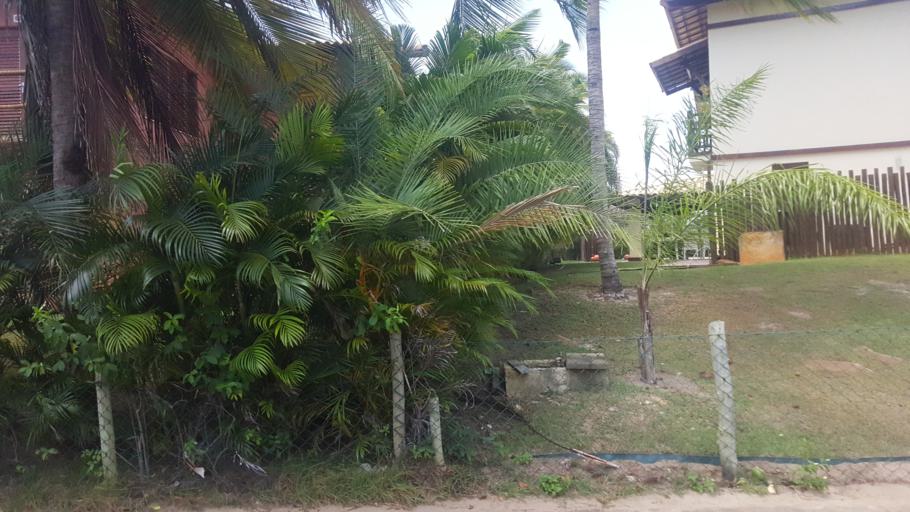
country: BR
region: Bahia
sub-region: Mata De Sao Joao
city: Mata de Sao Joao
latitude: -12.4815
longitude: -37.9601
